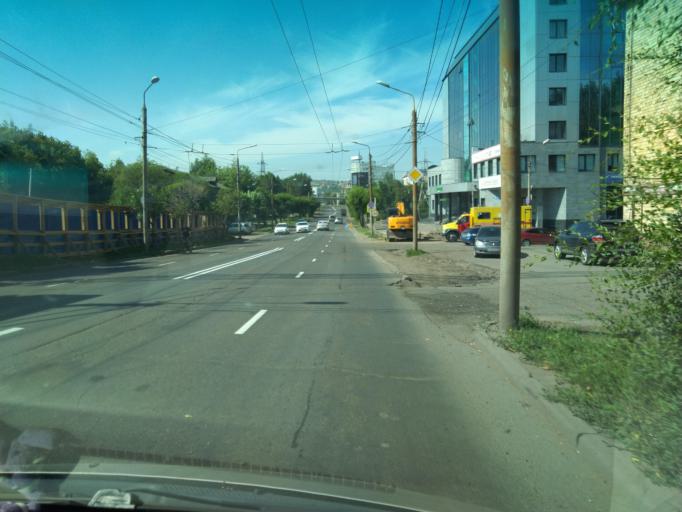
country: RU
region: Krasnoyarskiy
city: Krasnoyarsk
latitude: 56.0209
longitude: 92.8373
